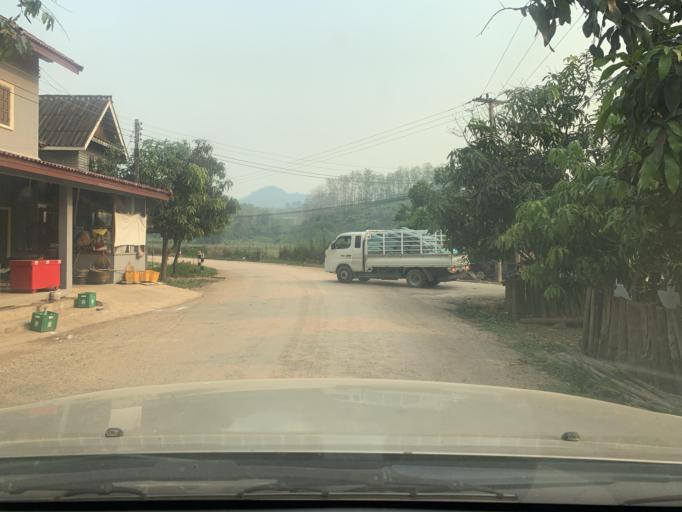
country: LA
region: Louangphabang
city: Louangphabang
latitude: 19.9158
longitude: 102.0746
